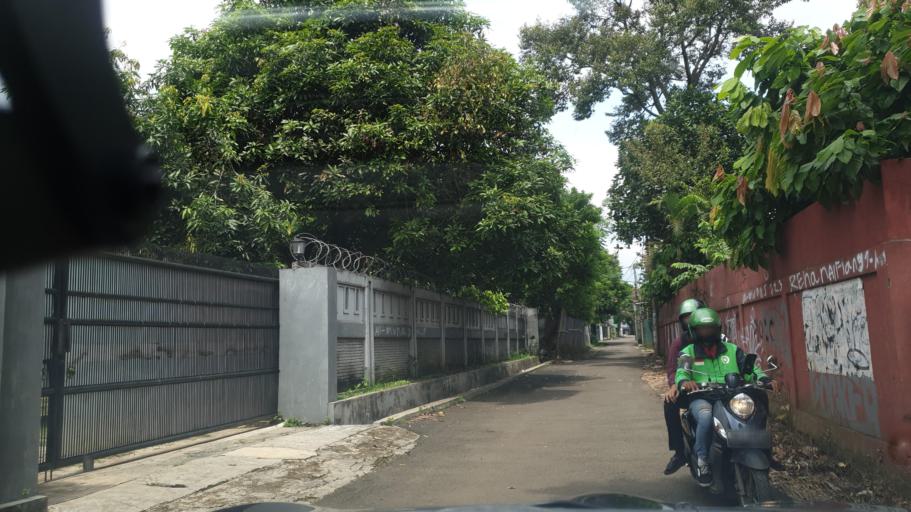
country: ID
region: West Java
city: Pamulang
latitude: -6.3370
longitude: 106.7715
